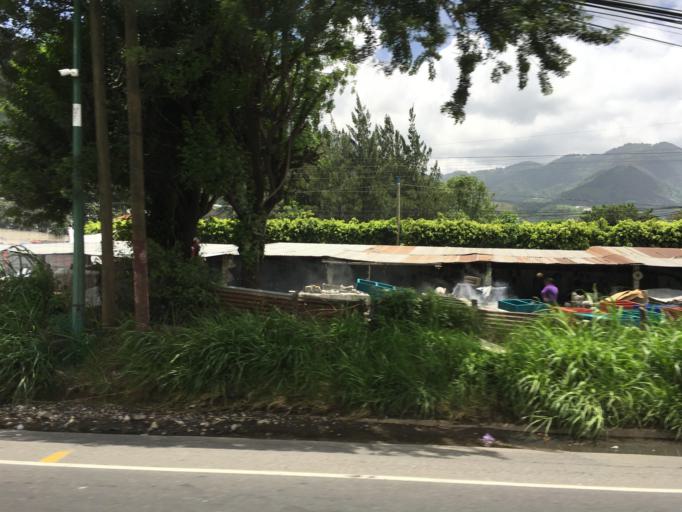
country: GT
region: Guatemala
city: Amatitlan
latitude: 14.4640
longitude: -90.6408
